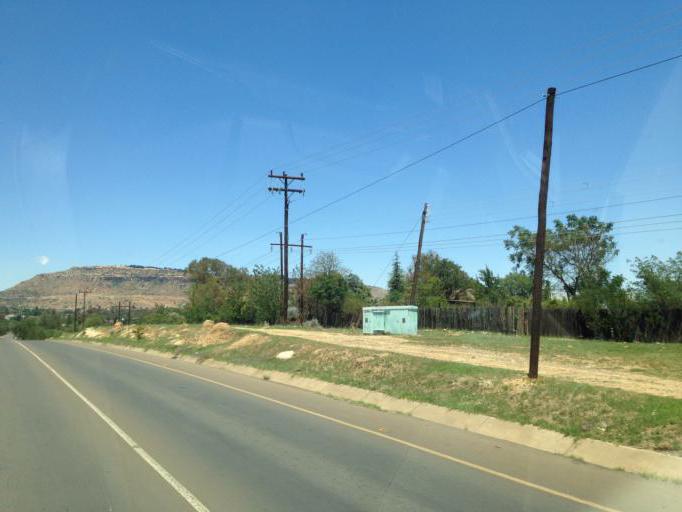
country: LS
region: Maseru
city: Maseru
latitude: -29.3052
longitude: 27.4661
